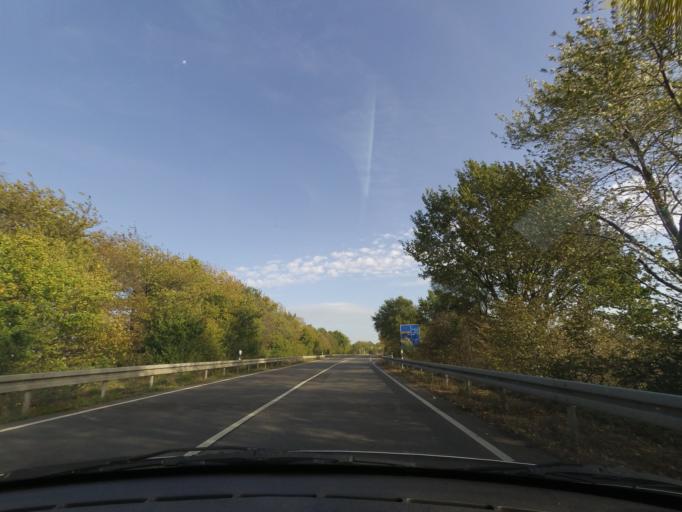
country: DE
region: North Rhine-Westphalia
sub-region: Regierungsbezirk Dusseldorf
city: Neubrueck
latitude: 51.1669
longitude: 6.6434
